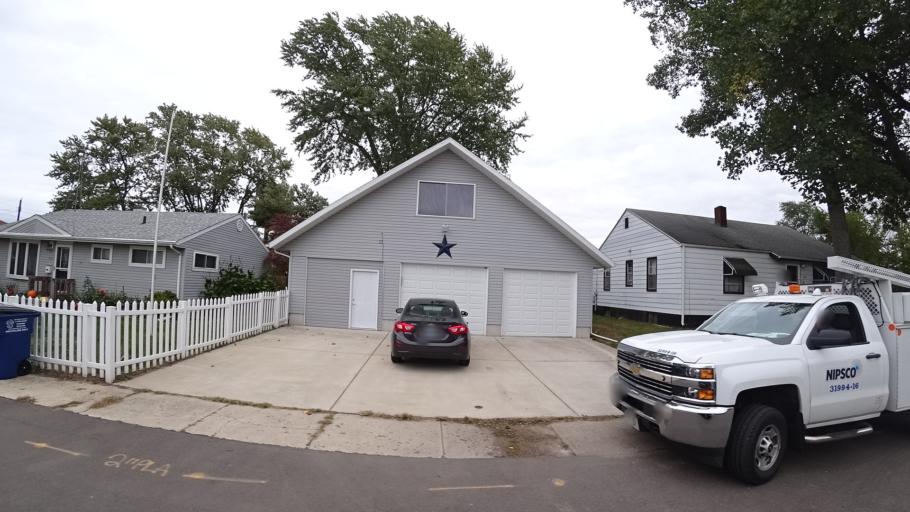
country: US
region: Indiana
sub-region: LaPorte County
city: Michigan City
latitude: 41.6996
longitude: -86.8953
